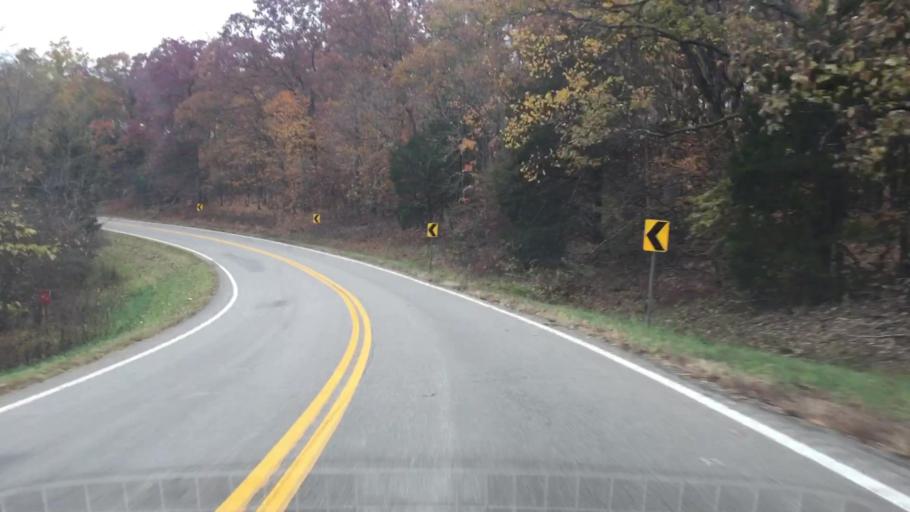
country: US
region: Missouri
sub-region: Gasconade County
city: Hermann
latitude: 38.7208
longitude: -91.6730
